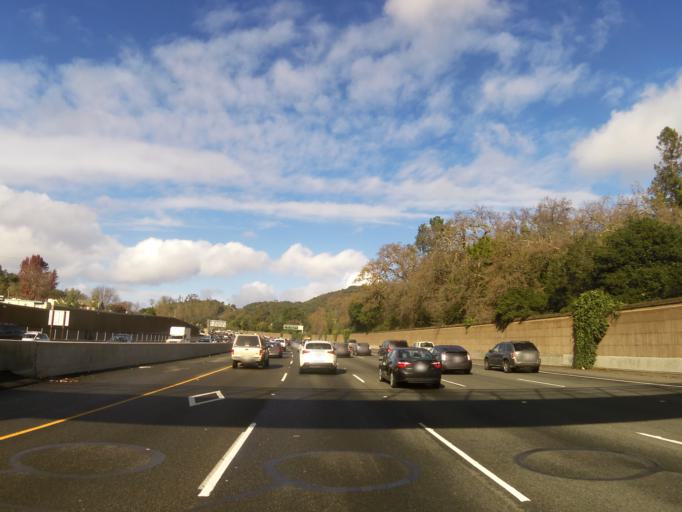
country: US
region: California
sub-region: Marin County
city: San Rafael
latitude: 37.9783
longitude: -122.5205
